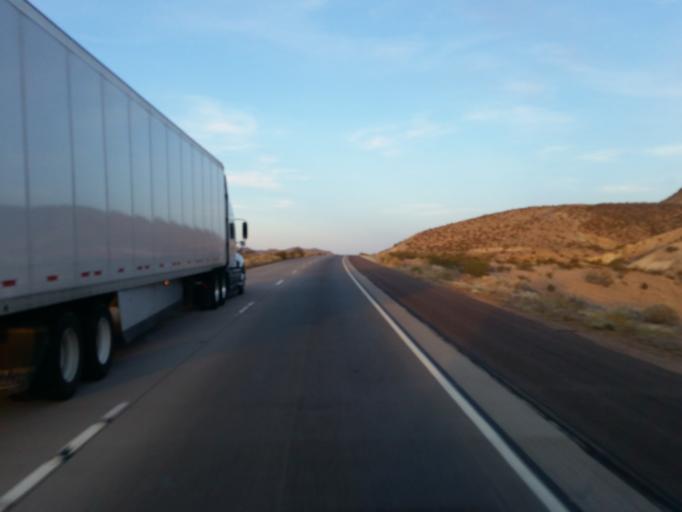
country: US
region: California
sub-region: San Bernardino County
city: Twentynine Palms
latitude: 34.7329
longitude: -115.8651
